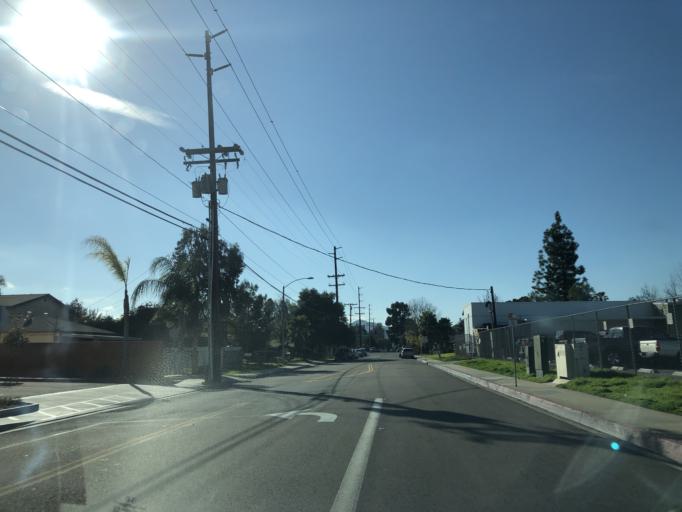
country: US
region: California
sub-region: San Diego County
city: Escondido
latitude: 33.1332
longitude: -117.0887
